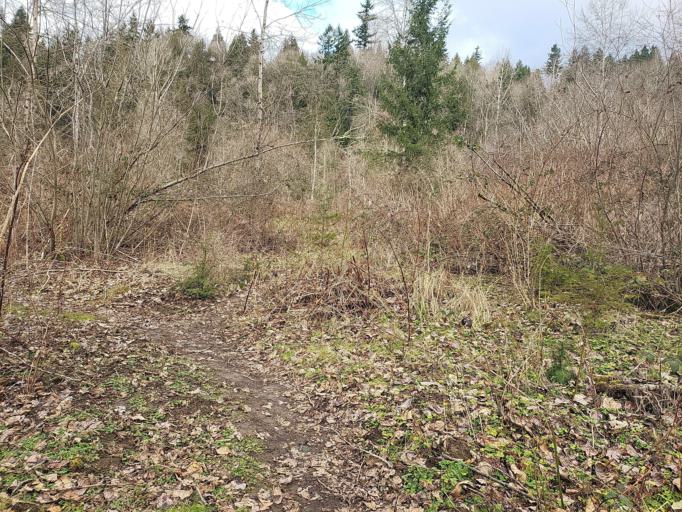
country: US
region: Washington
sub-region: King County
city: Fairwood
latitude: 47.4696
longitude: -122.1519
